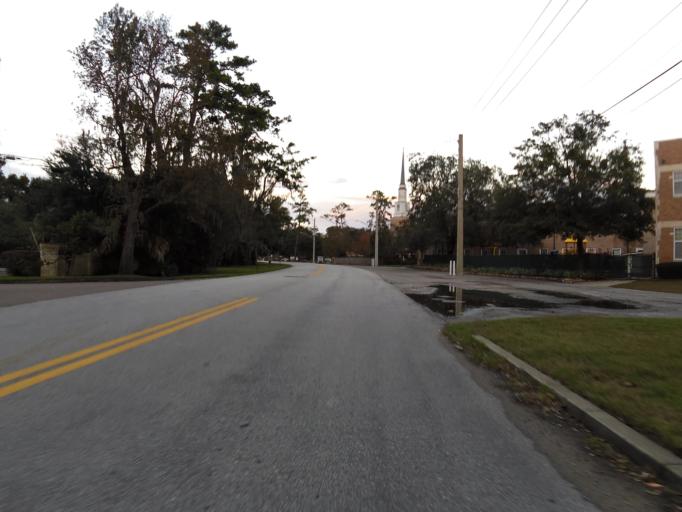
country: US
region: Florida
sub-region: Duval County
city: Jacksonville
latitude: 30.2922
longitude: -81.6499
